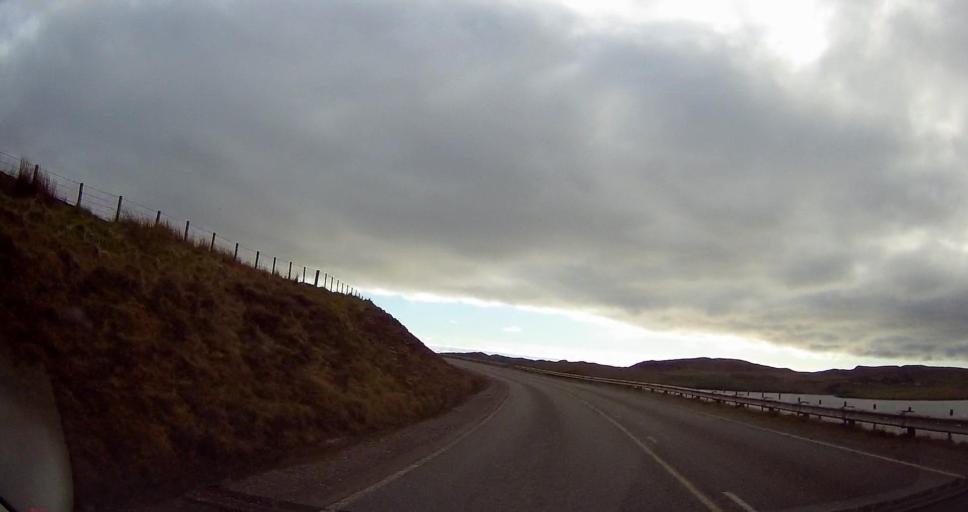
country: GB
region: Scotland
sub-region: Shetland Islands
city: Lerwick
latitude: 60.4076
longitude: -1.3404
